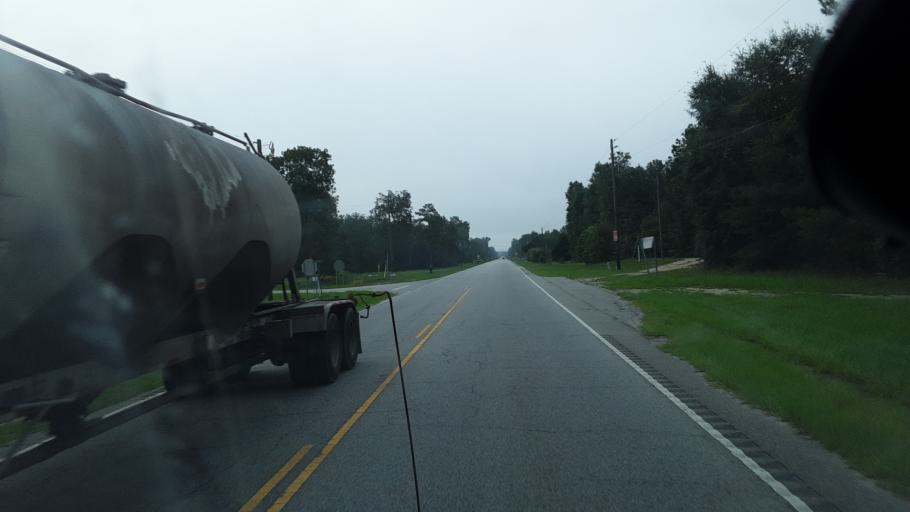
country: US
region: South Carolina
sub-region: Florence County
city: Johnsonville
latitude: 33.8925
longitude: -79.3844
